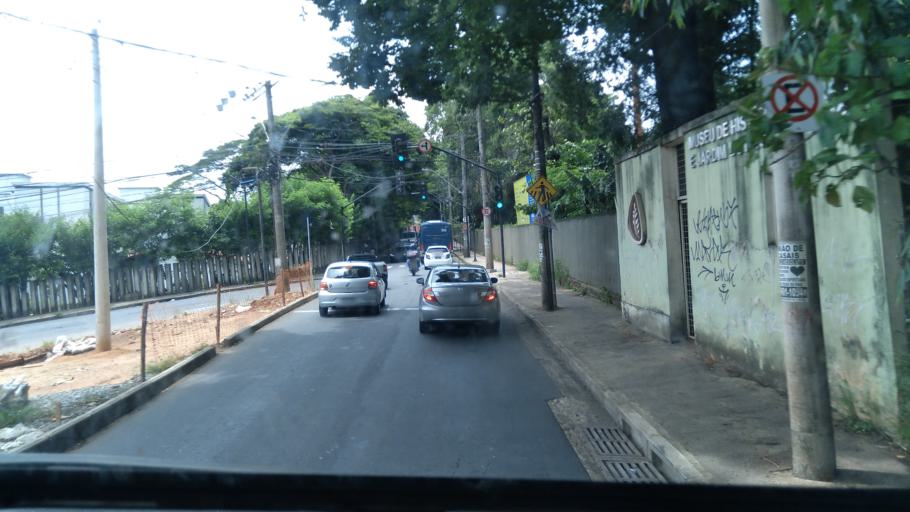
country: BR
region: Minas Gerais
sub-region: Belo Horizonte
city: Belo Horizonte
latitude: -19.8952
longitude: -43.9123
